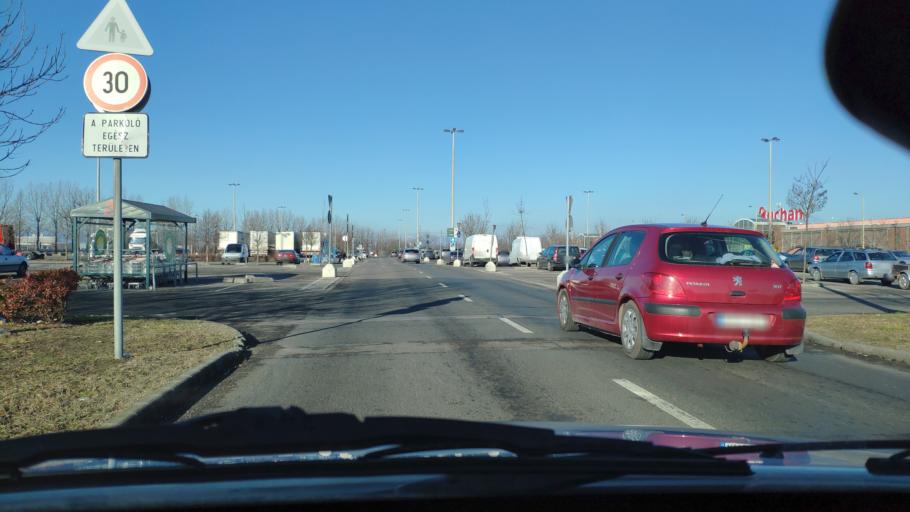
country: HU
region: Budapest
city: Budapest XVIII. keruelet
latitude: 47.4168
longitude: 19.1578
